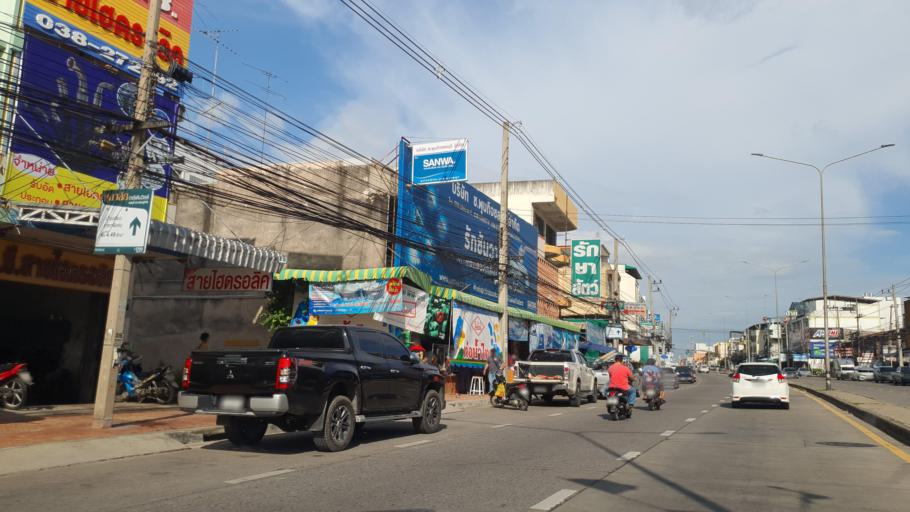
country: TH
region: Chon Buri
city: Chon Buri
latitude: 13.3591
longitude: 100.9924
